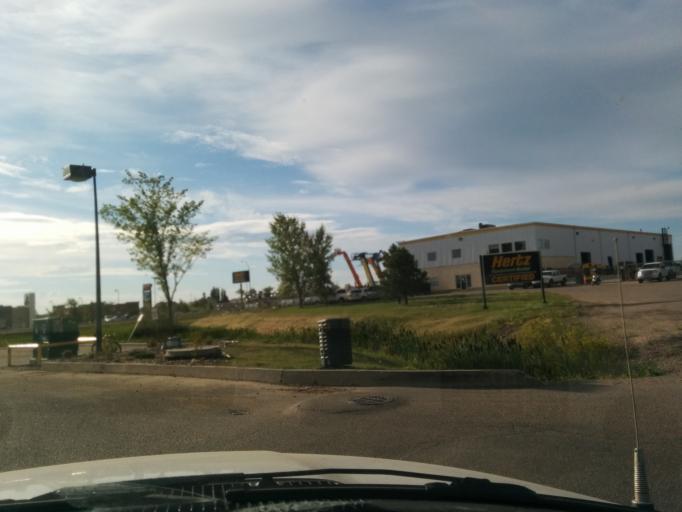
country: CA
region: Alberta
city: Grande Prairie
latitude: 55.1514
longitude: -118.8225
